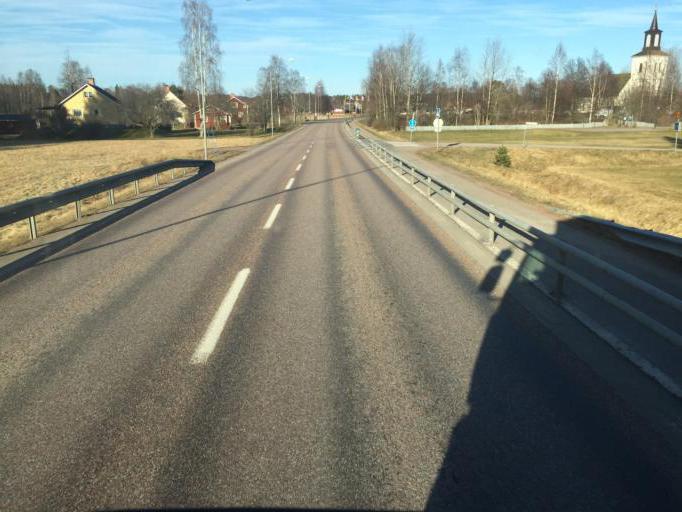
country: SE
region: Dalarna
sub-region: Gagnefs Kommun
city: Mockfjard
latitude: 60.5083
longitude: 14.7942
